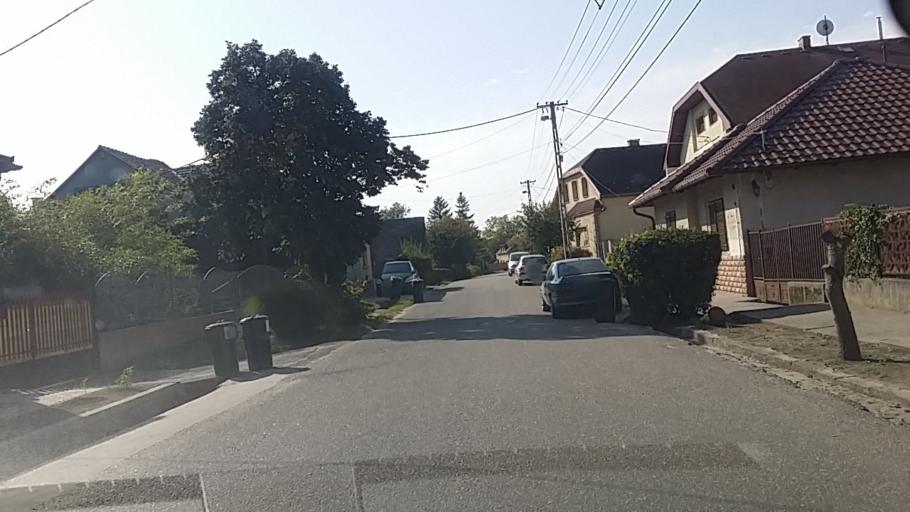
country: HU
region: Pest
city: Fot
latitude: 47.6066
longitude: 19.2041
